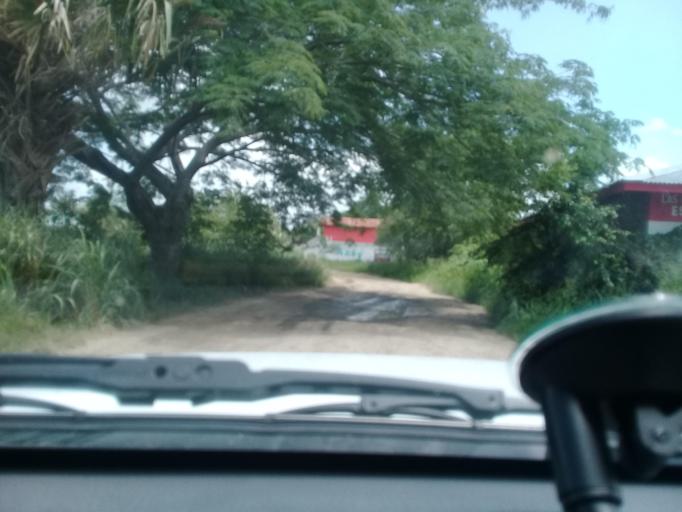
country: MX
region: Veracruz
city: Moralillo
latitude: 22.1811
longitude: -98.0173
